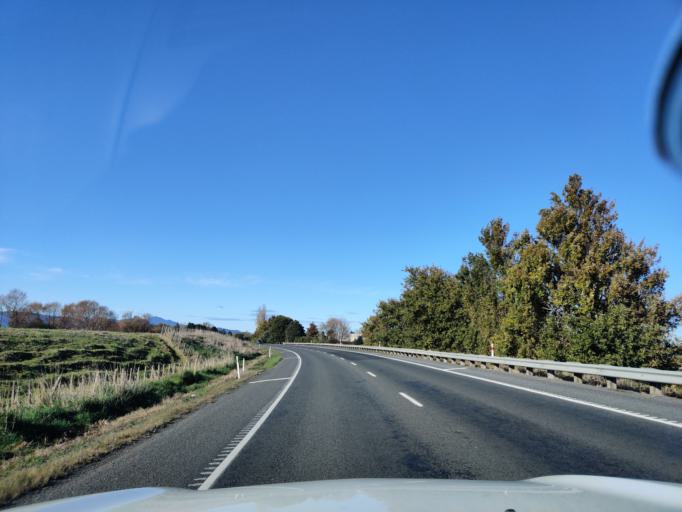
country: NZ
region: Waikato
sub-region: Hauraki District
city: Paeroa
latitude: -37.3306
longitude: 175.6085
